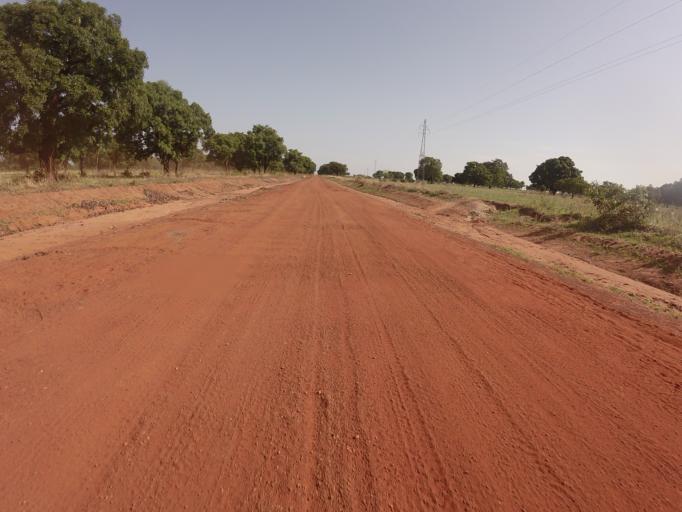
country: GH
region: Upper East
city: Bawku
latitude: 10.7750
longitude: -0.1935
